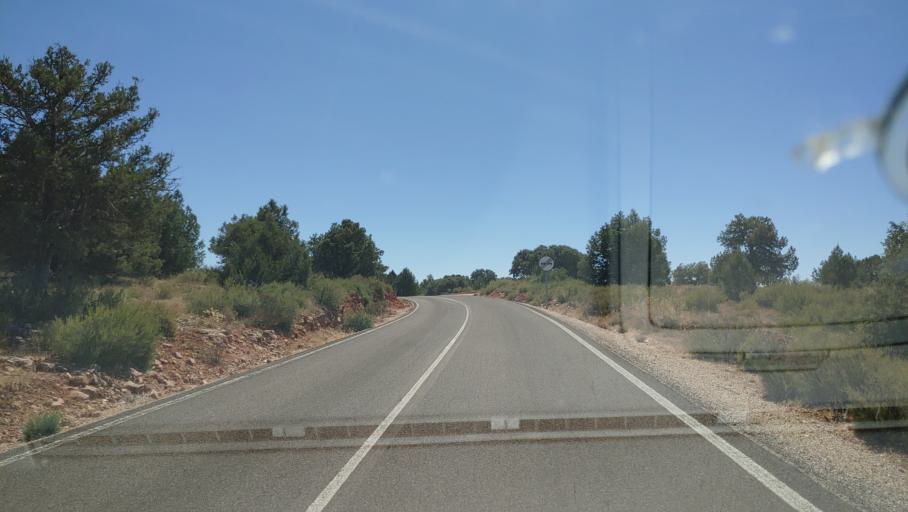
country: ES
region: Castille-La Mancha
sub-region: Provincia de Albacete
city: Ossa de Montiel
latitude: 38.8627
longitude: -2.8008
